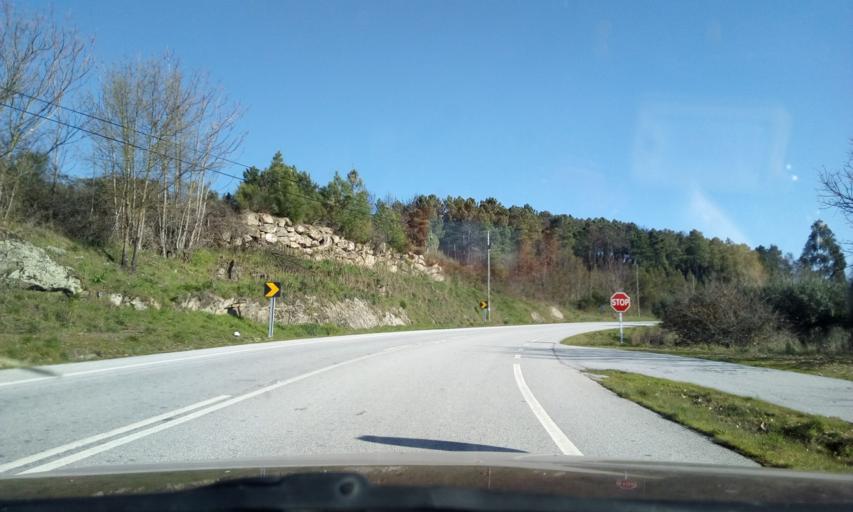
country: PT
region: Guarda
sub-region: Fornos de Algodres
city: Fornos de Algodres
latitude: 40.6206
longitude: -7.5112
